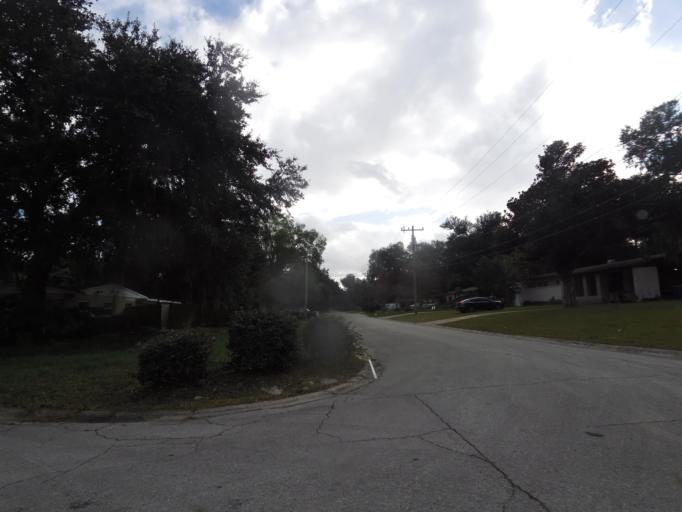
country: US
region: Florida
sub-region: Duval County
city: Jacksonville
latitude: 30.3263
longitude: -81.5914
